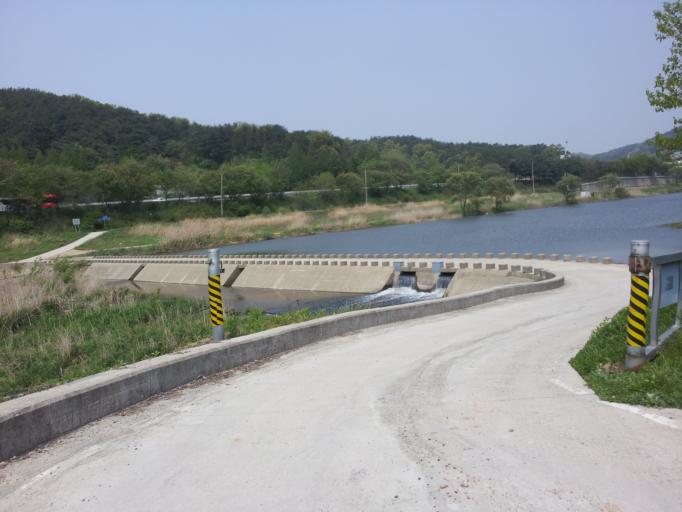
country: KR
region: Daejeon
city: Daejeon
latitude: 36.2593
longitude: 127.2842
